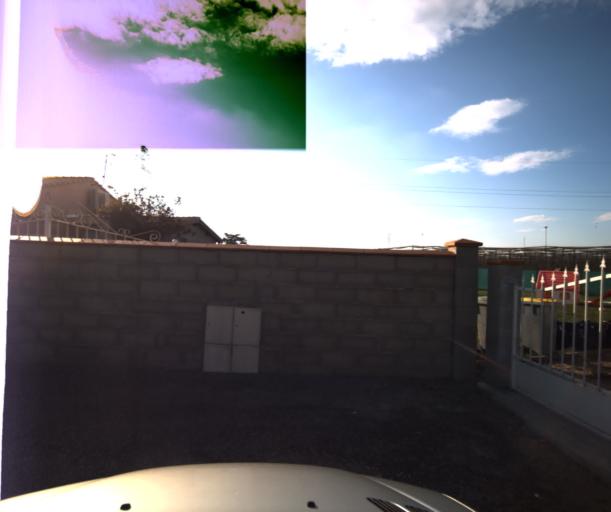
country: FR
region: Midi-Pyrenees
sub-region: Departement du Tarn-et-Garonne
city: Bressols
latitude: 43.9651
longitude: 1.3284
